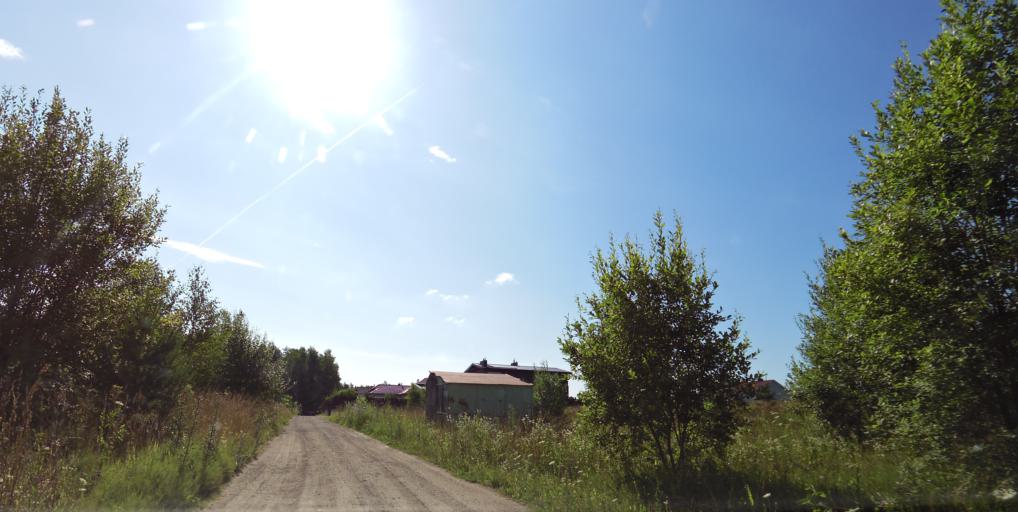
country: LT
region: Vilnius County
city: Pilaite
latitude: 54.6899
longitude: 25.1788
